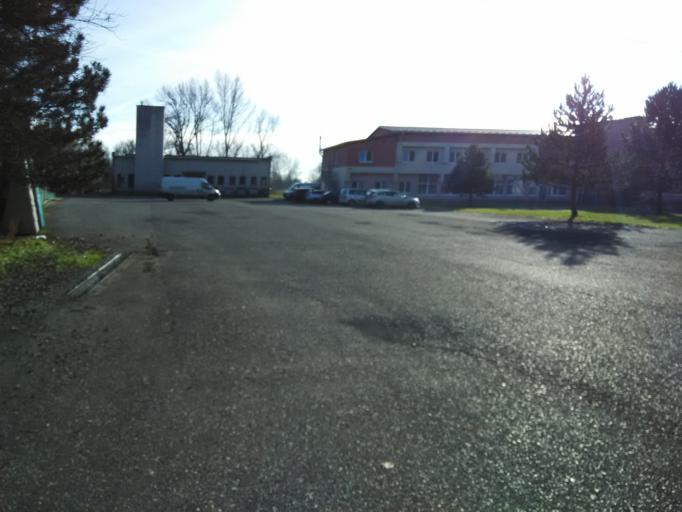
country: SK
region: Nitriansky
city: Tlmace
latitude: 48.2903
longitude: 18.5210
